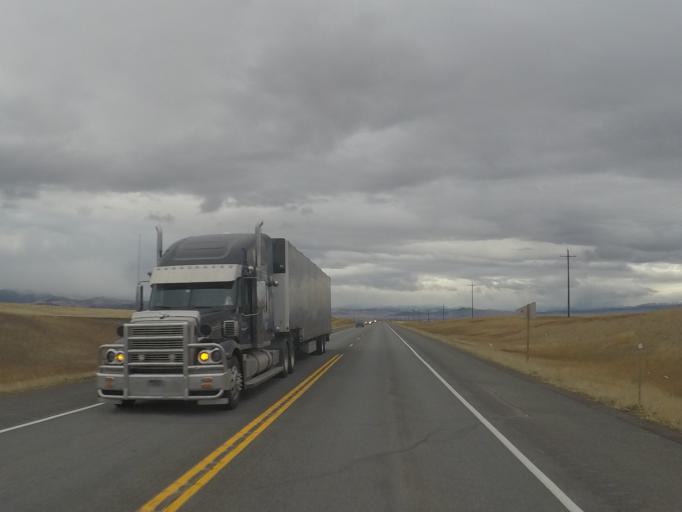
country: US
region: Montana
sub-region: Lewis and Clark County
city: East Helena
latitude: 46.5646
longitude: -111.7990
